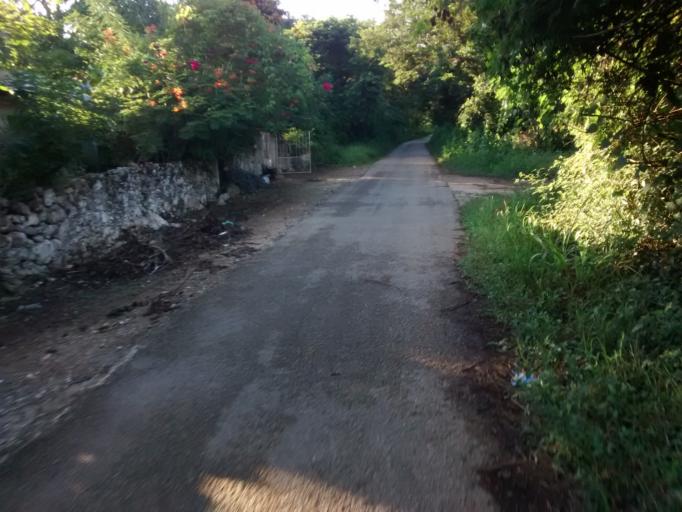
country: MX
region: Yucatan
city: Valladolid
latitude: 20.7269
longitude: -88.2318
